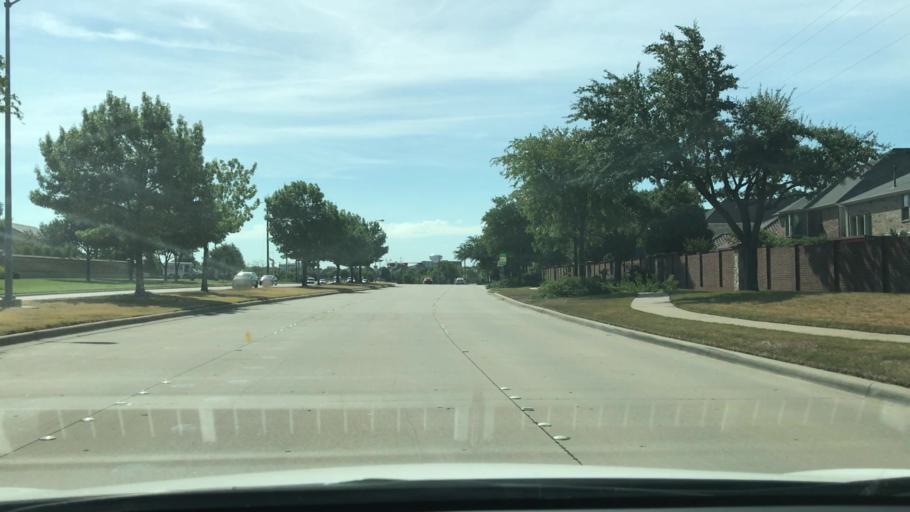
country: US
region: Texas
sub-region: Denton County
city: The Colony
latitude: 33.0677
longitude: -96.8408
